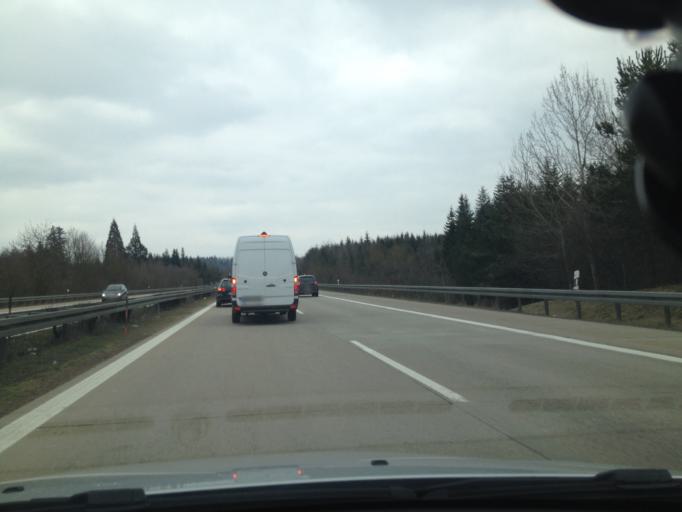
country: DE
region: Baden-Wuerttemberg
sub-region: Regierungsbezirk Stuttgart
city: Ellenberg
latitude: 49.0054
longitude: 10.1943
